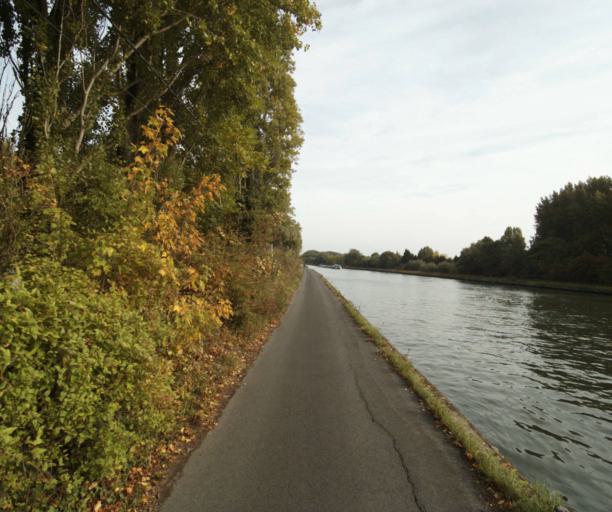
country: FR
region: Nord-Pas-de-Calais
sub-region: Departement du Nord
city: Bauvin
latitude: 50.5361
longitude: 2.9005
